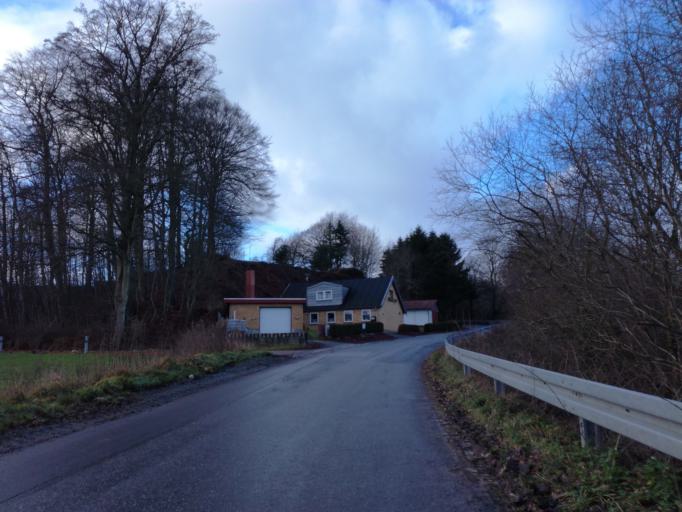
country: DK
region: South Denmark
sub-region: Fredericia Kommune
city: Taulov
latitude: 55.5662
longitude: 9.6210
